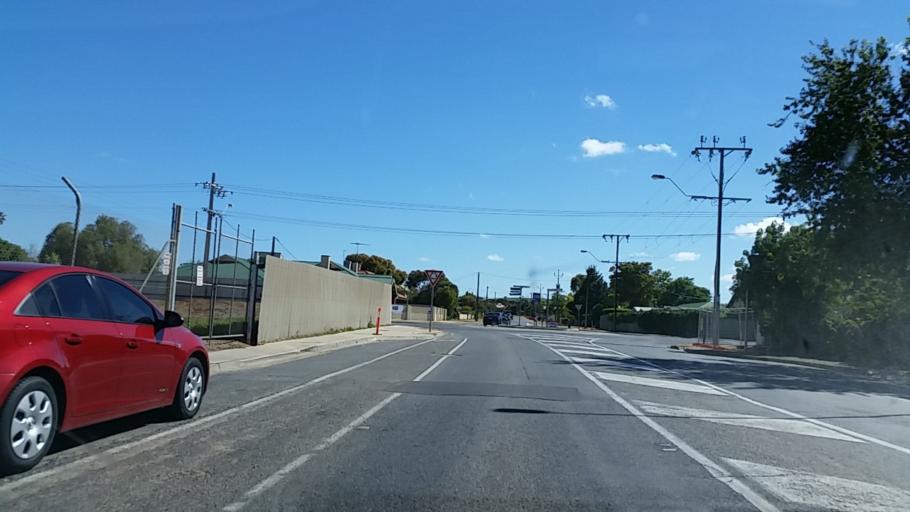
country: AU
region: South Australia
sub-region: Alexandrina
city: Strathalbyn
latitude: -35.2612
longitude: 138.8907
